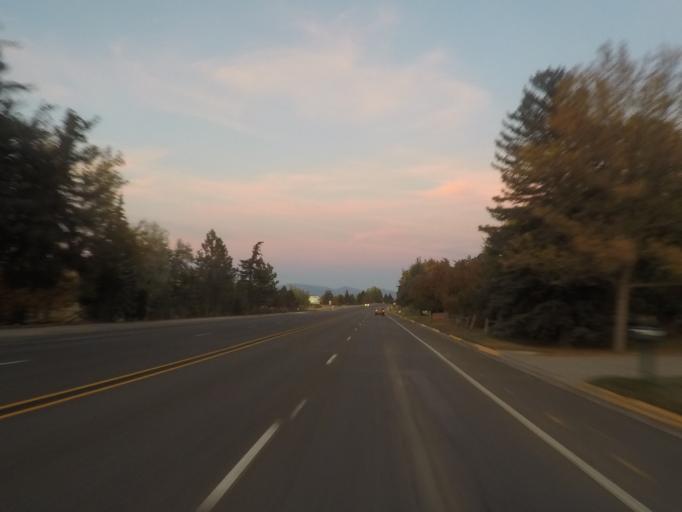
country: US
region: Montana
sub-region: Lewis and Clark County
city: Helena West Side
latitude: 46.5962
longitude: -112.1076
